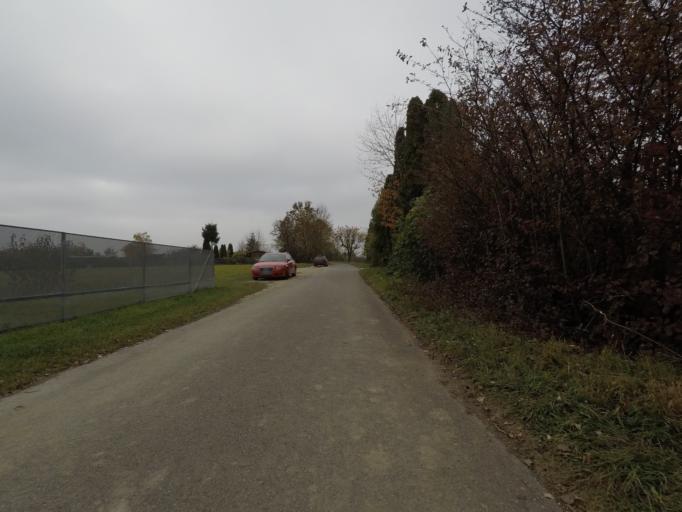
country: DE
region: Baden-Wuerttemberg
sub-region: Tuebingen Region
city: Reutlingen
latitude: 48.5153
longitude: 9.2107
